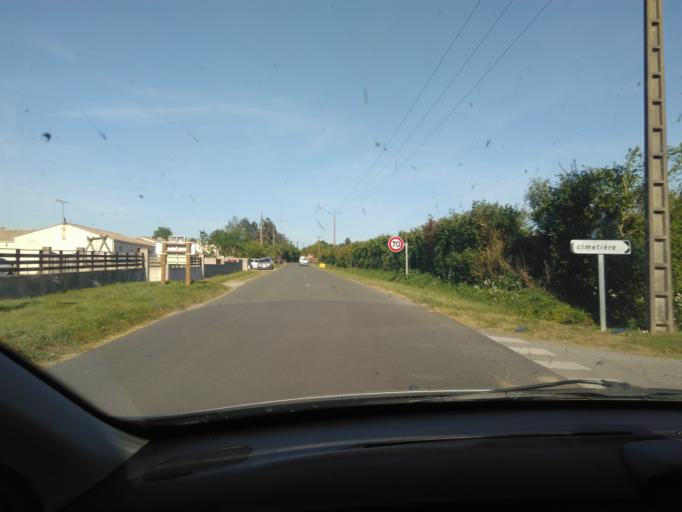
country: FR
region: Pays de la Loire
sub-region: Departement de la Vendee
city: Saint-Florent-des-Bois
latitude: 46.5748
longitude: -1.3414
